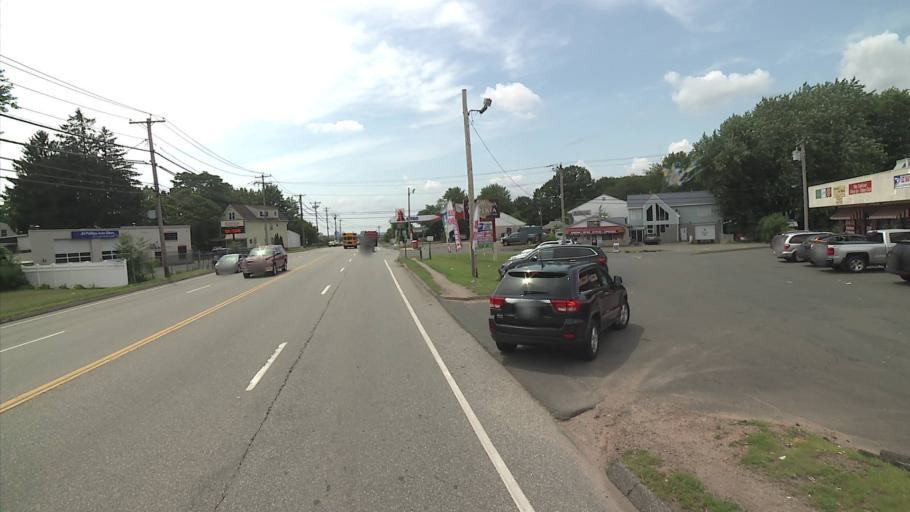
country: US
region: Connecticut
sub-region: New Haven County
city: East Haven
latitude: 41.3210
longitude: -72.8646
